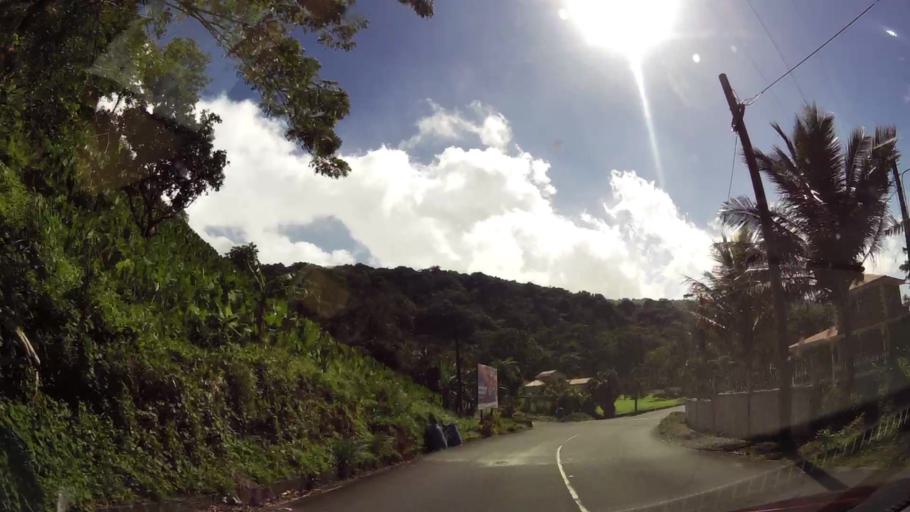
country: DM
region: Saint Paul
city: Pont Casse
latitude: 15.3615
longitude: -61.3546
